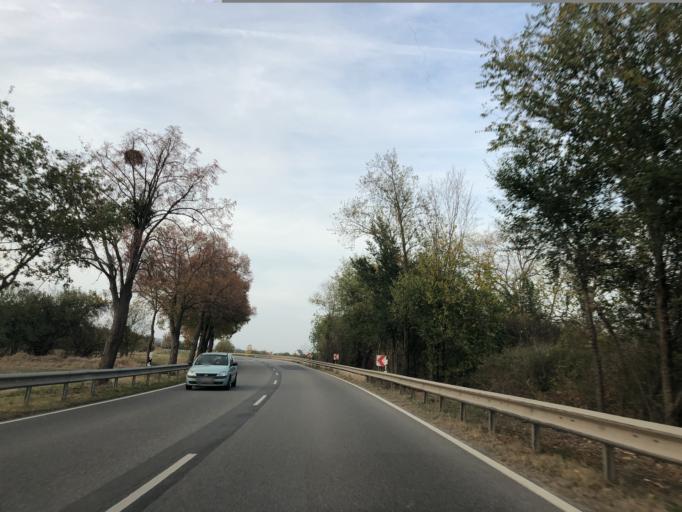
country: DE
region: Rheinland-Pfalz
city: Guntersblum
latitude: 49.7820
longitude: 8.3546
